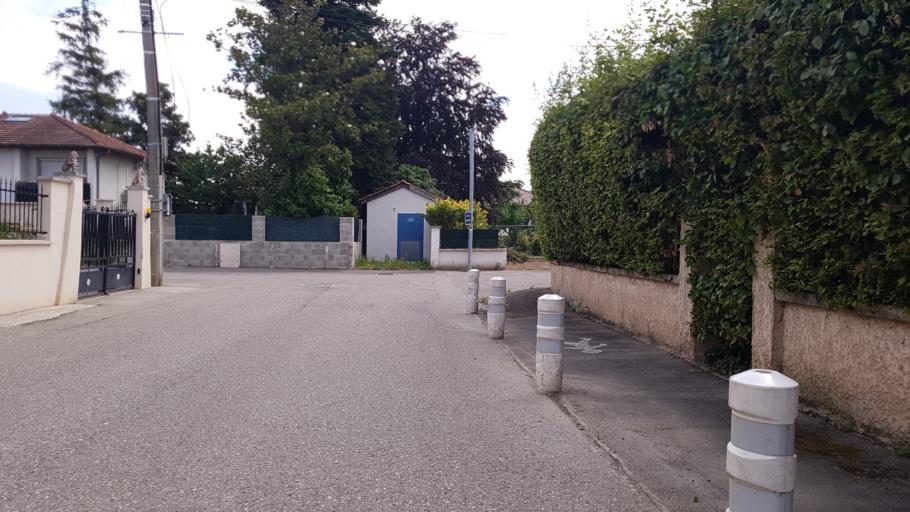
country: FR
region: Rhone-Alpes
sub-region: Departement du Rhone
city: Genas
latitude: 45.7280
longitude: 5.0154
